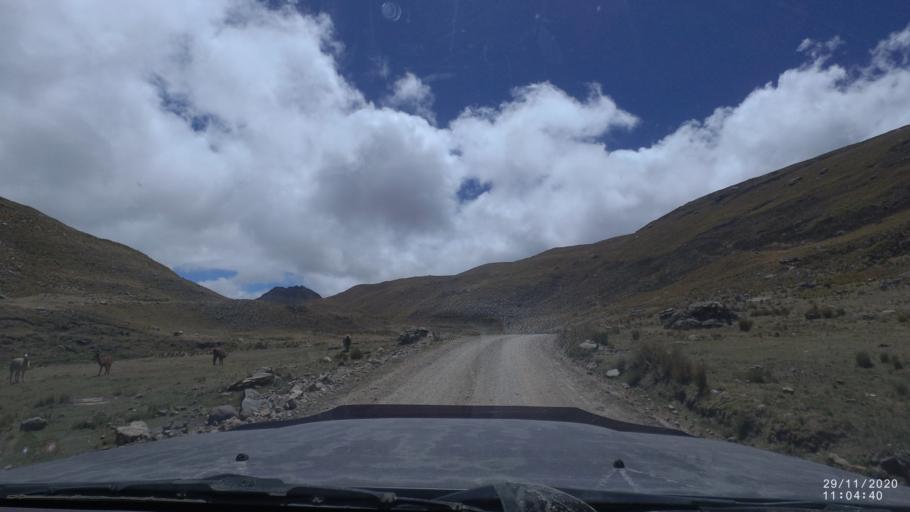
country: BO
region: Cochabamba
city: Cochabamba
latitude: -17.1882
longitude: -66.2154
